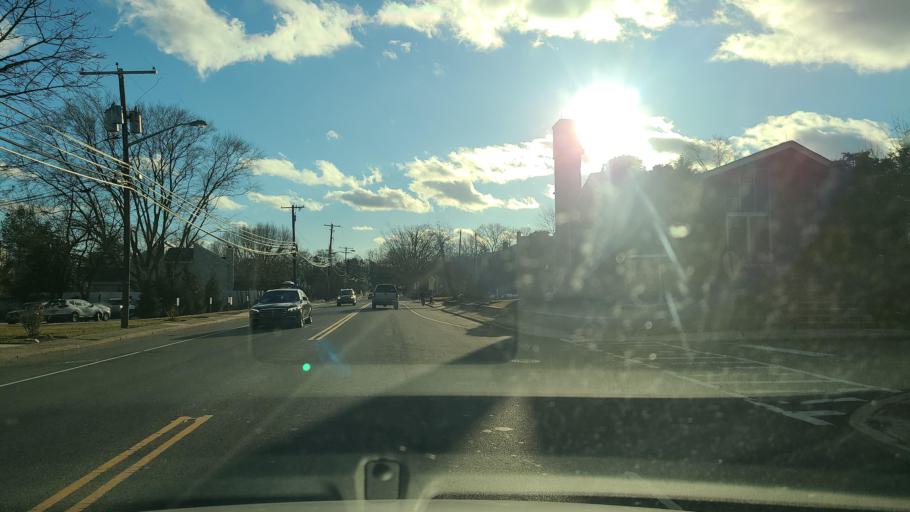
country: US
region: New Jersey
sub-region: Union County
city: Springfield
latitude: 40.6924
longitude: -74.3217
